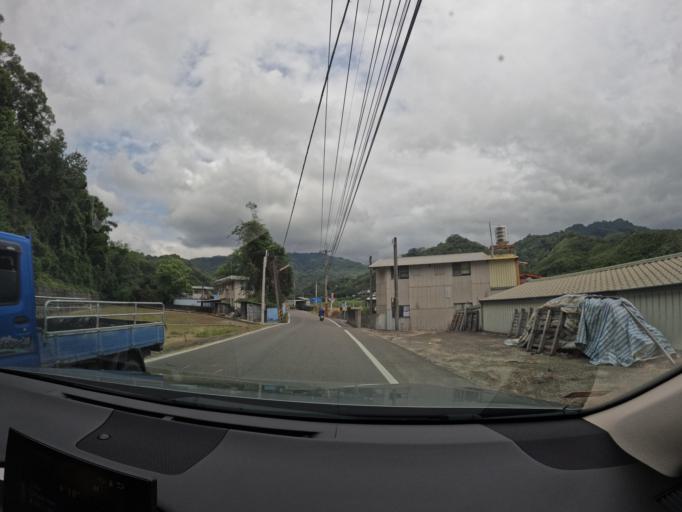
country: TW
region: Taiwan
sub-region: Miaoli
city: Miaoli
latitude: 24.4273
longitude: 120.8747
